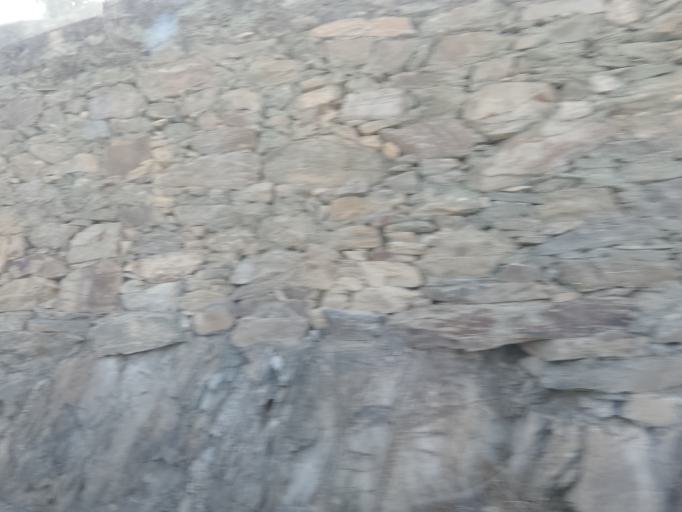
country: PT
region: Vila Real
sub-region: Sabrosa
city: Vilela
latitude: 41.1828
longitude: -7.5524
